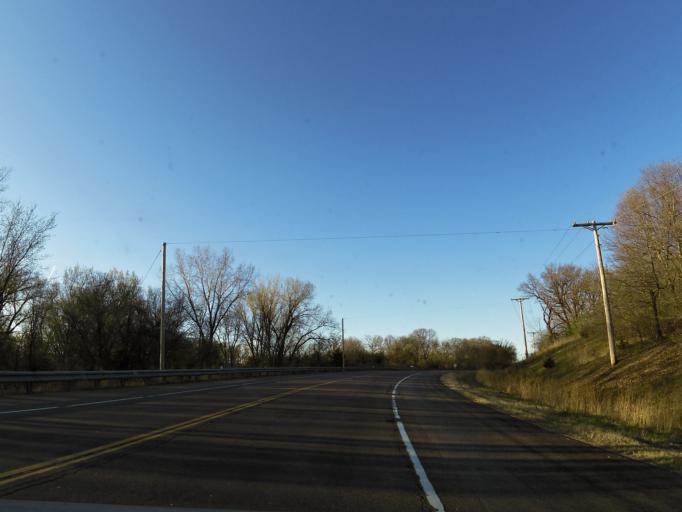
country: US
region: Wisconsin
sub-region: Pierce County
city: Prescott
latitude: 44.6472
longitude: -92.7722
